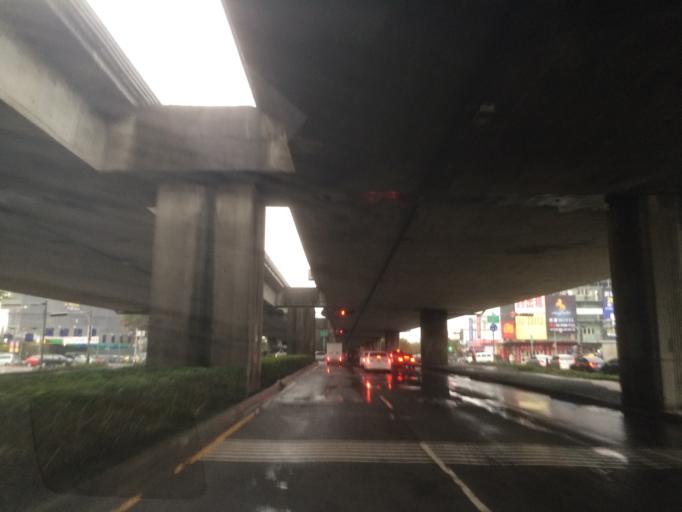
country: TW
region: Taiwan
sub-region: Taichung City
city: Taichung
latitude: 24.1462
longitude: 120.6231
